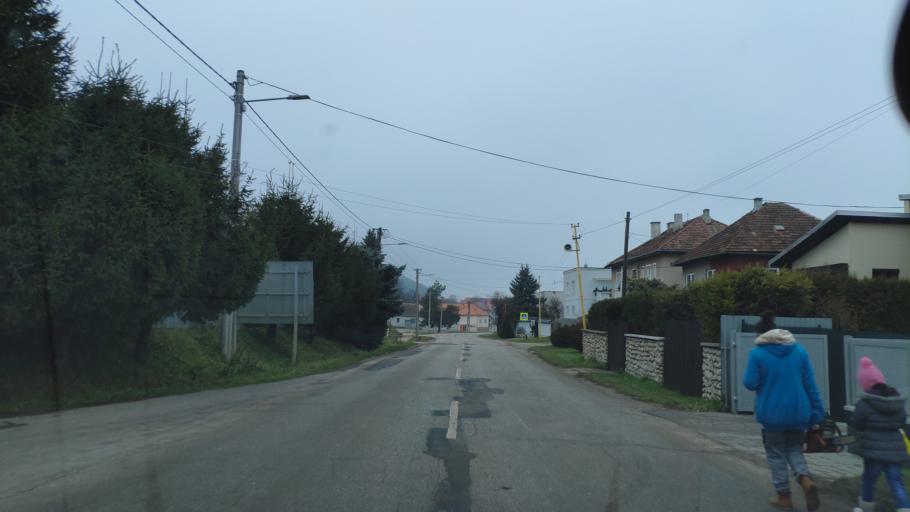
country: SK
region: Kosicky
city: Dobsina
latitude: 48.6532
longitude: 20.3661
